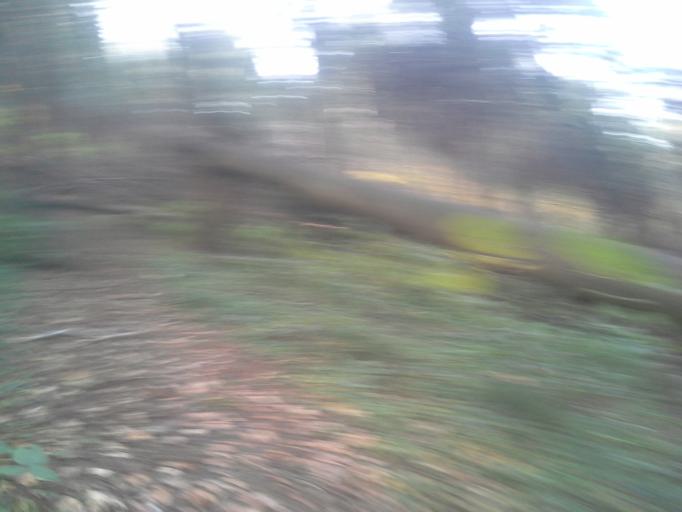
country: RU
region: Moskovskaya
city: Krasnoznamensk
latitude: 55.5827
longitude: 37.0162
